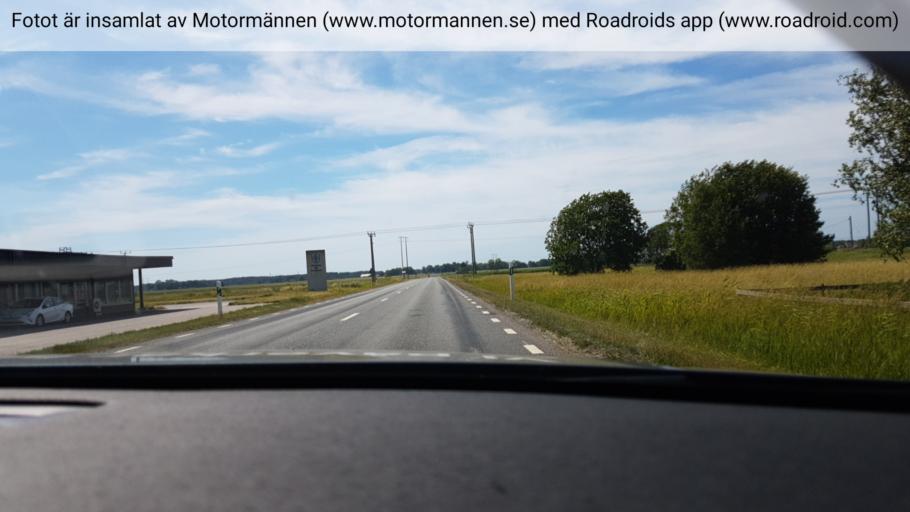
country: SE
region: Vaestra Goetaland
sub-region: Toreboda Kommun
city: Toereboda
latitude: 58.7048
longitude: 14.1127
